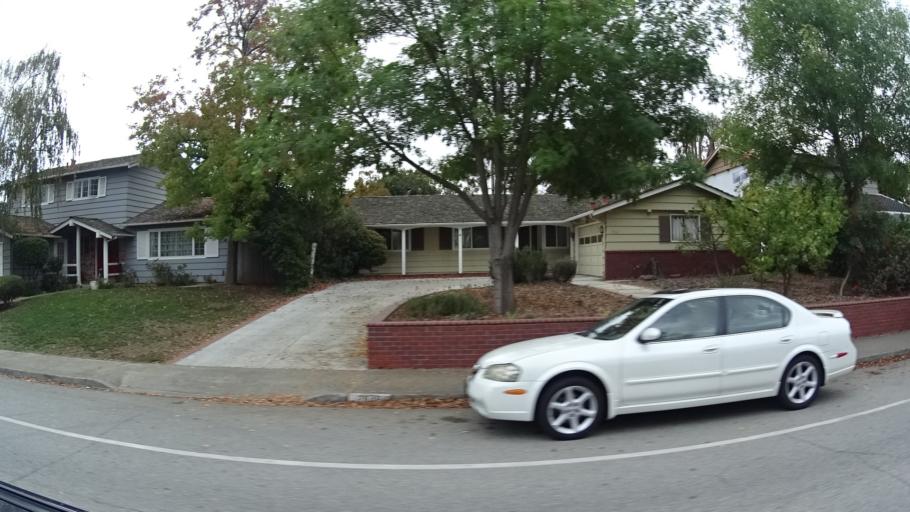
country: US
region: California
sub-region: Santa Clara County
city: Santa Clara
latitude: 37.3324
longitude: -121.9767
